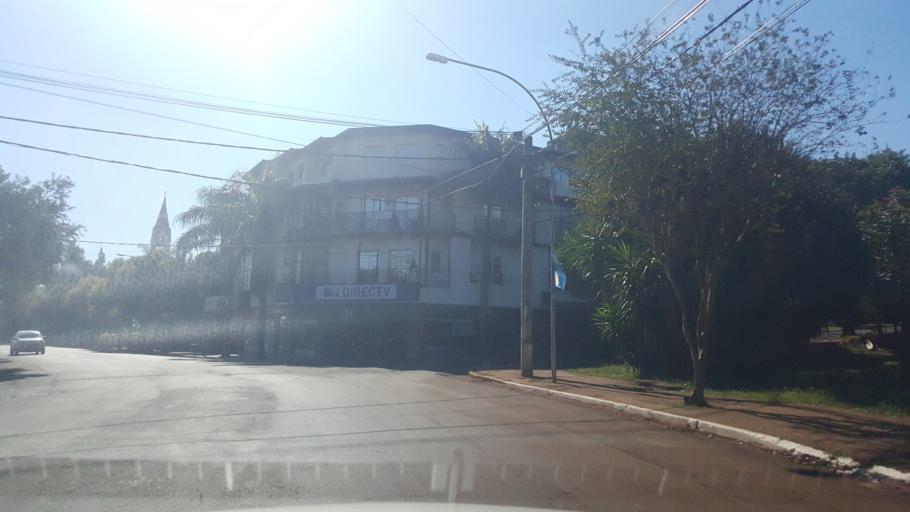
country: AR
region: Misiones
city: Puerto Rico
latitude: -26.8194
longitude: -55.0270
